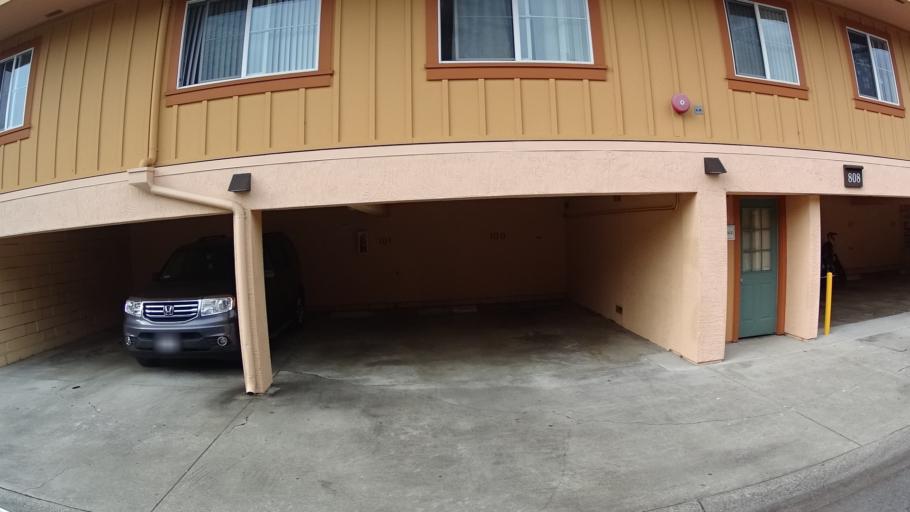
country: US
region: California
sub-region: San Mateo County
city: South San Francisco
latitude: 37.6540
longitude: -122.4301
